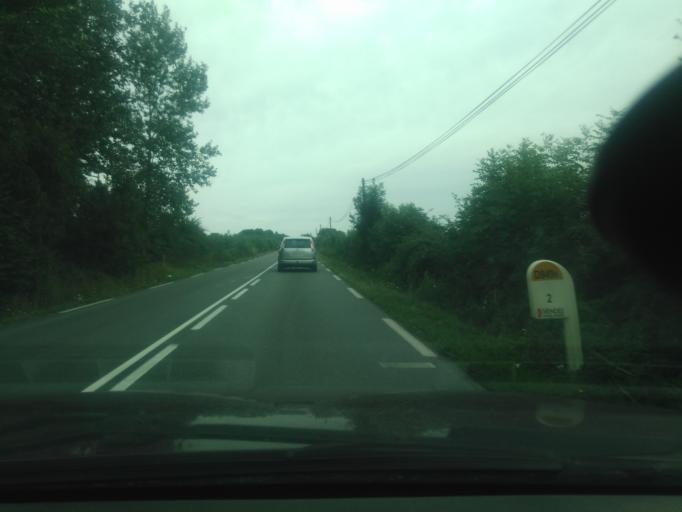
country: FR
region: Pays de la Loire
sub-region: Departement de la Vendee
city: Saint-Pierre-du-Chemin
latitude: 46.6518
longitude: -0.6711
